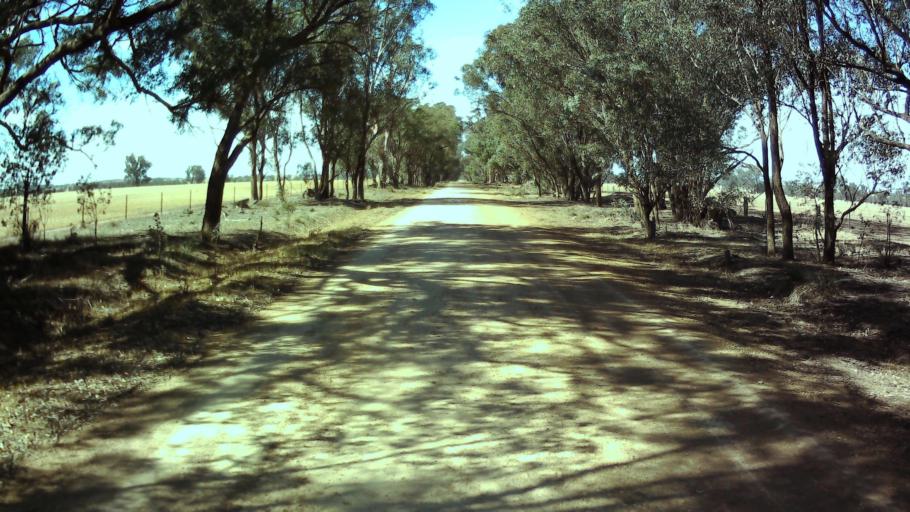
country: AU
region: New South Wales
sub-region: Weddin
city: Grenfell
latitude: -34.0475
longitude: 148.3145
